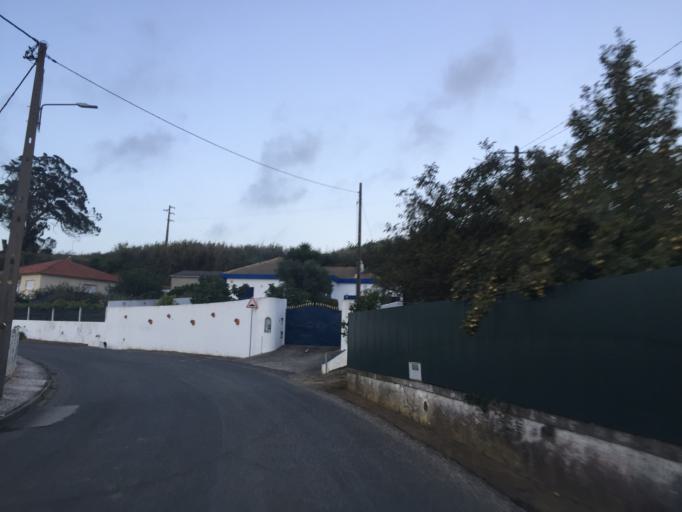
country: PT
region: Leiria
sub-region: Bombarral
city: Bombarral
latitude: 39.2849
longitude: -9.2167
